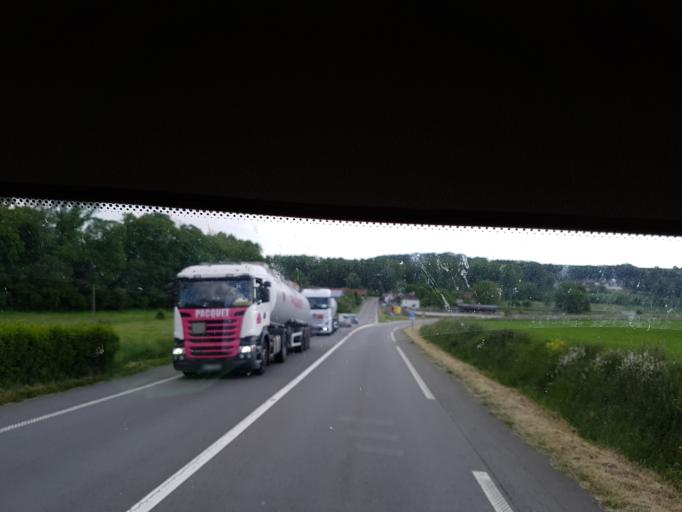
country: FR
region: Nord-Pas-de-Calais
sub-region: Departement du Pas-de-Calais
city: Marconnelle
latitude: 50.2821
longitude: 1.9888
